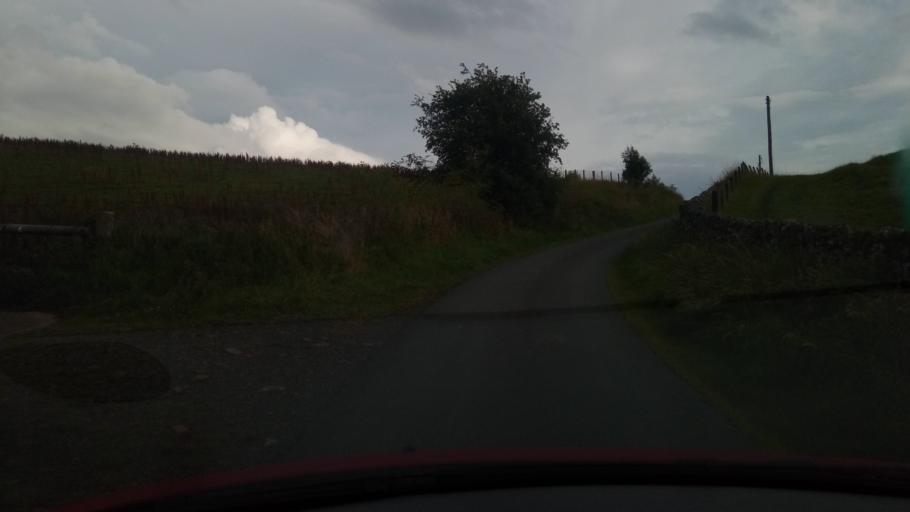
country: GB
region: Scotland
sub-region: The Scottish Borders
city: Hawick
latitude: 55.4175
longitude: -2.7789
